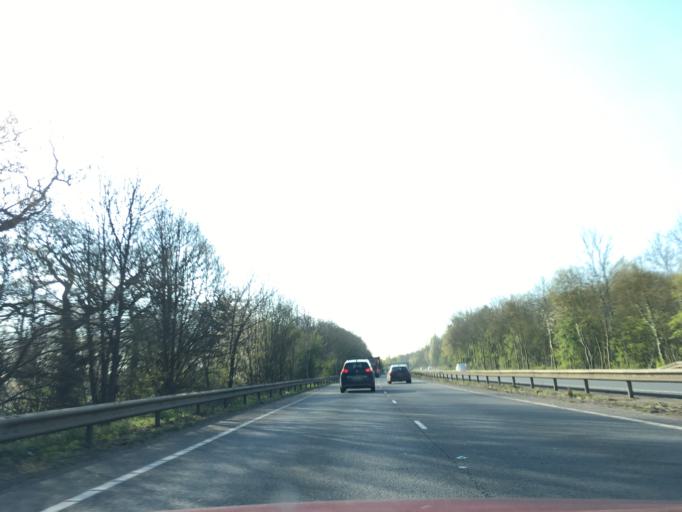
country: GB
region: England
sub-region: Milton Keynes
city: Stony Stratford
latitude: 52.0587
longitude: -0.8405
